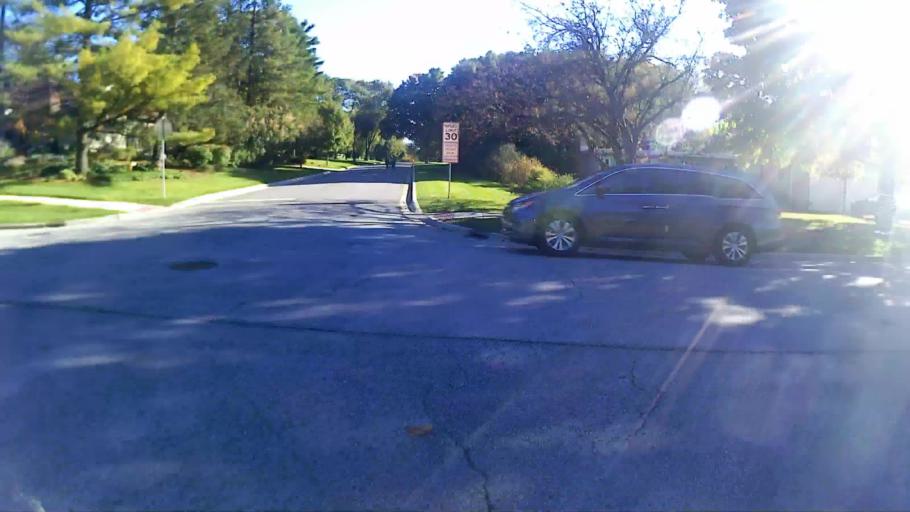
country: US
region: Illinois
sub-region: DuPage County
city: Wheaton
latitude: 41.8552
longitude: -88.1040
